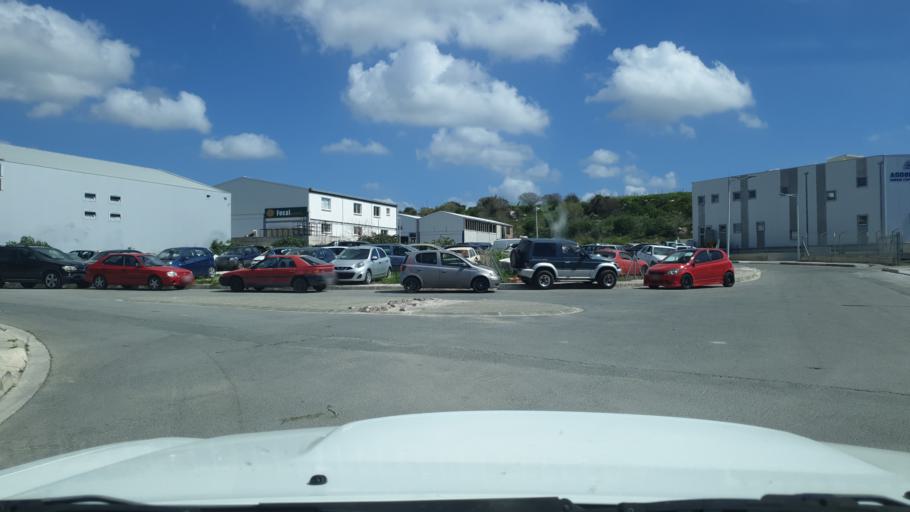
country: CY
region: Pafos
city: Paphos
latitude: 34.7527
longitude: 32.4602
